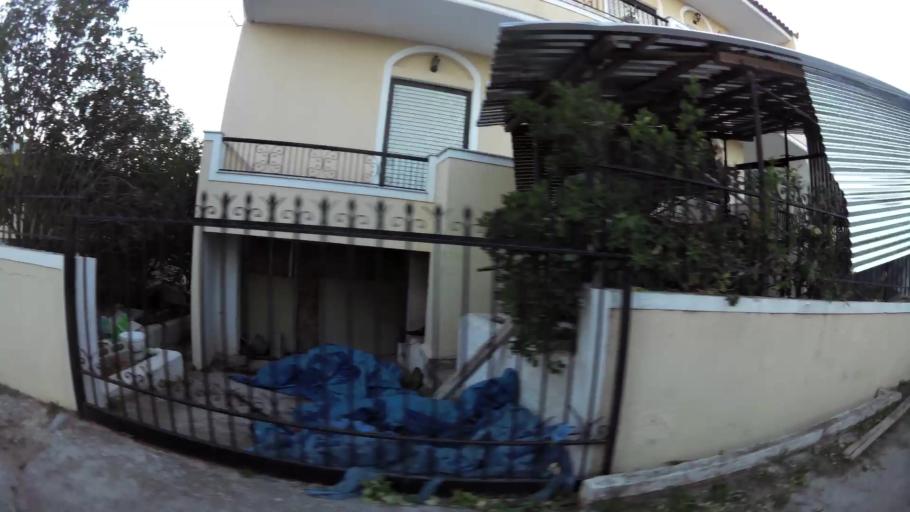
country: GR
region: Attica
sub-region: Nomarchia Anatolikis Attikis
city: Paiania
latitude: 37.9692
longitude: 23.8400
